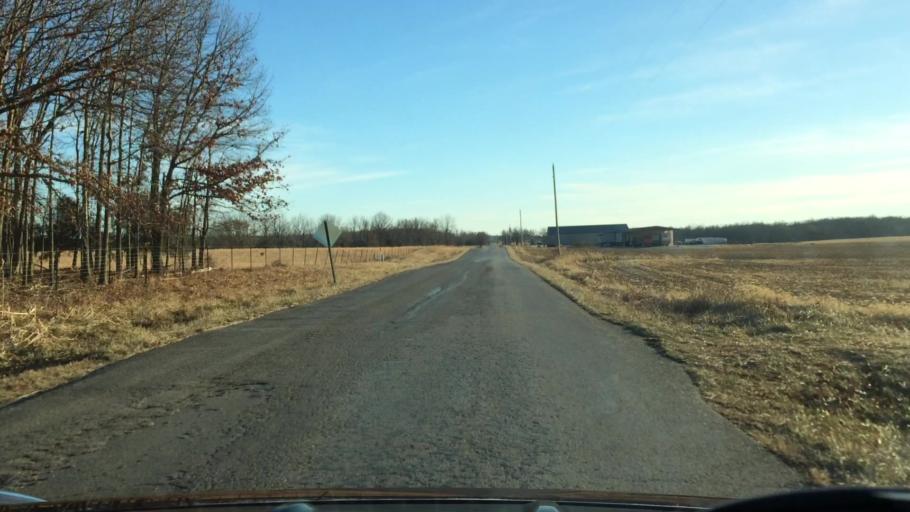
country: US
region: Missouri
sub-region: Webster County
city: Marshfield
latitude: 37.3375
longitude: -92.9840
